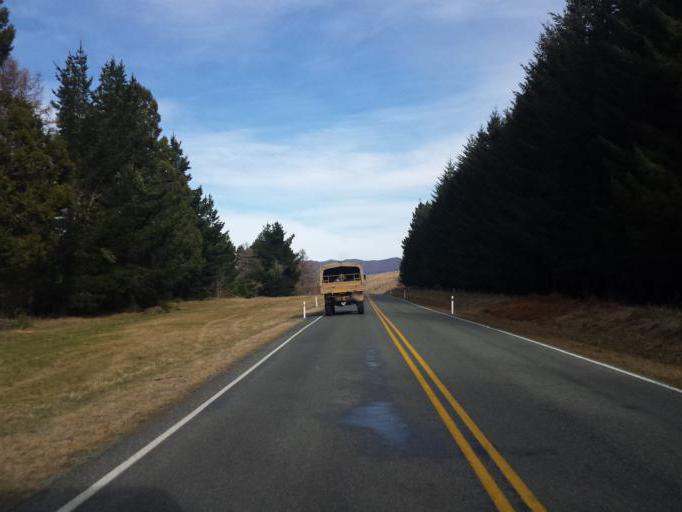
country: NZ
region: Canterbury
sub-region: Timaru District
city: Pleasant Point
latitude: -44.0480
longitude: 170.6817
